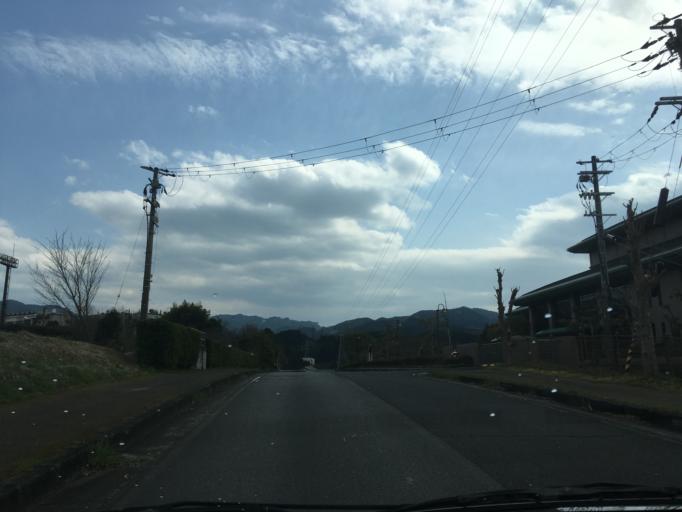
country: JP
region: Nara
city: Gose
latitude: 34.4512
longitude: 135.7908
